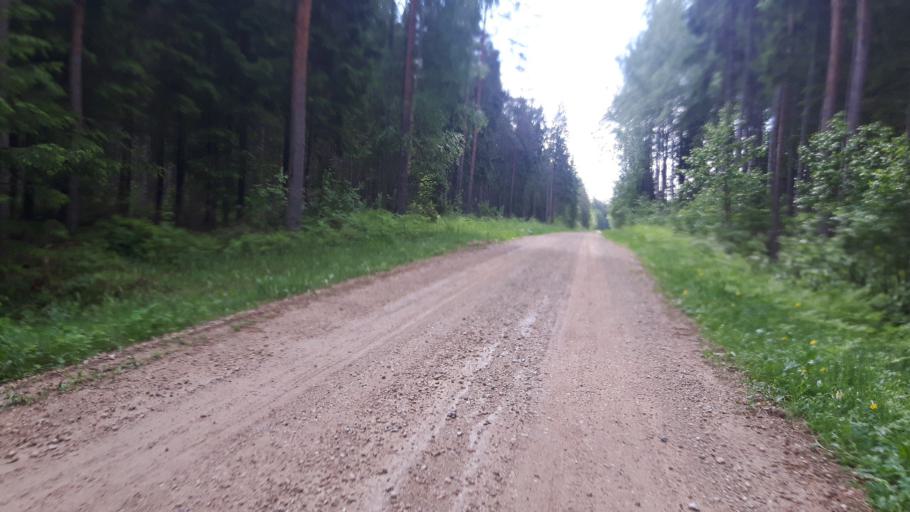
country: EE
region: Paernumaa
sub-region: Vaendra vald (alev)
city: Vandra
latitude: 58.7271
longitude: 25.0326
